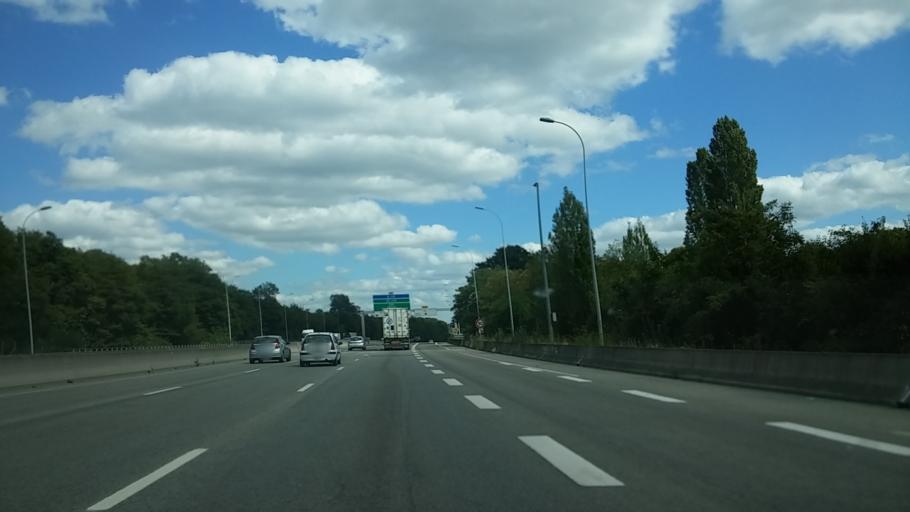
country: FR
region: Ile-de-France
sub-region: Departement des Yvelines
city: Buc
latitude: 48.7898
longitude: 2.1230
